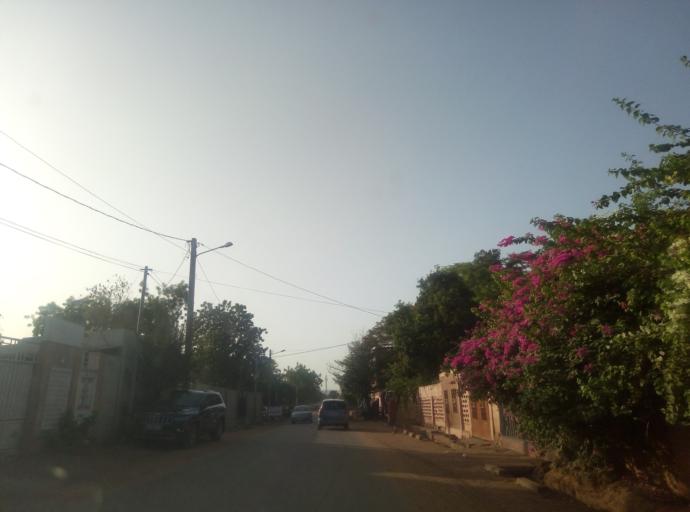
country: ML
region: Bamako
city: Bamako
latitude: 12.6076
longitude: -7.9718
